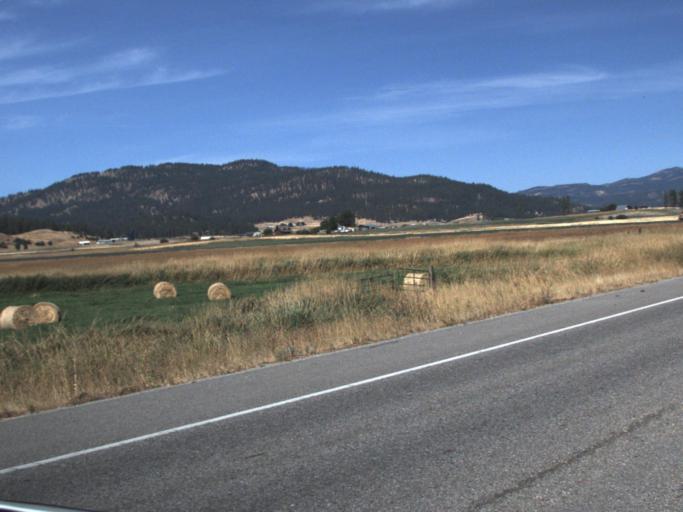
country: US
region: Washington
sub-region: Stevens County
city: Chewelah
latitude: 48.2194
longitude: -117.7153
